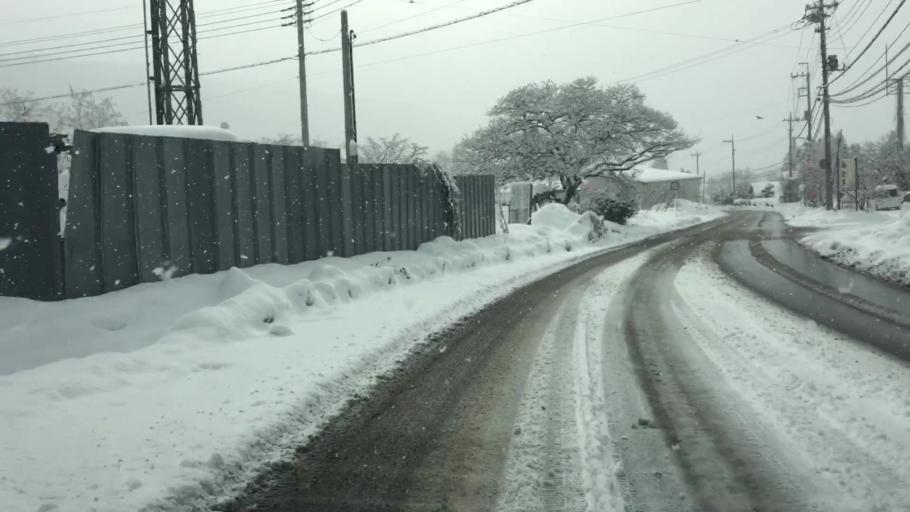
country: JP
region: Gunma
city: Numata
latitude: 36.7173
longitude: 139.0648
